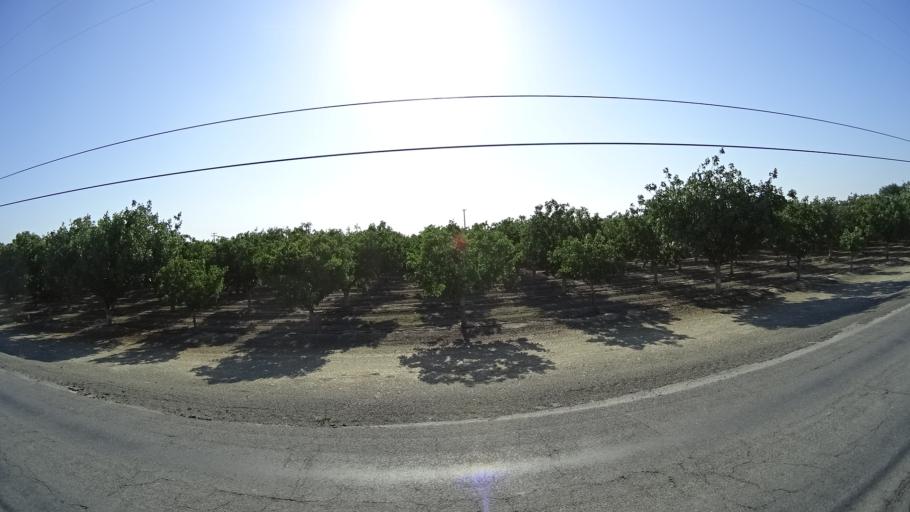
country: US
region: California
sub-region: Kings County
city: Home Garden
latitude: 36.3179
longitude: -119.5652
